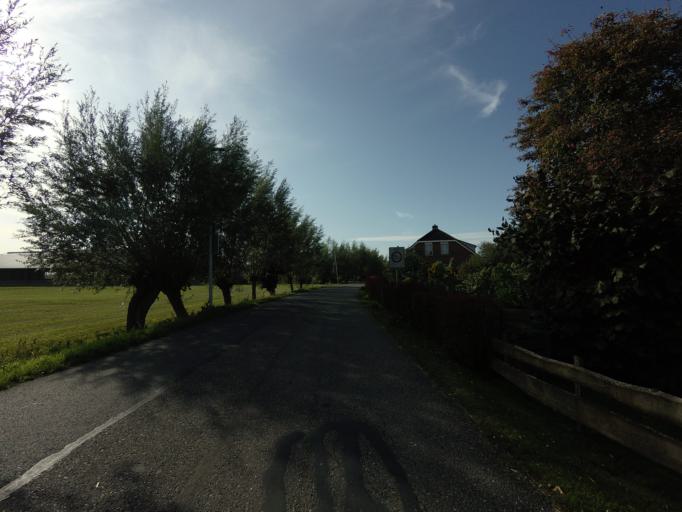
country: NL
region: Utrecht
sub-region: Gemeente Lopik
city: Lopik
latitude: 51.9394
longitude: 4.9671
